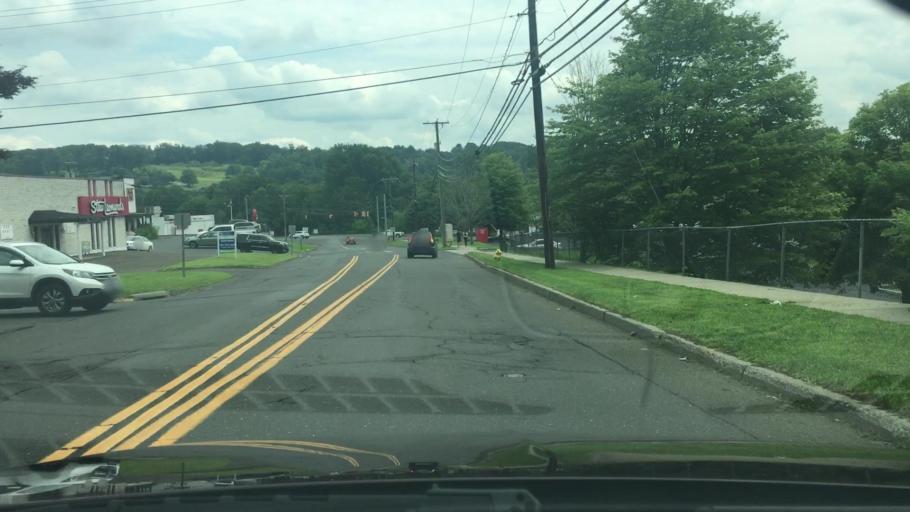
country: US
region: Connecticut
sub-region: Fairfield County
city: Danbury
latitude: 41.4272
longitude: -73.4211
